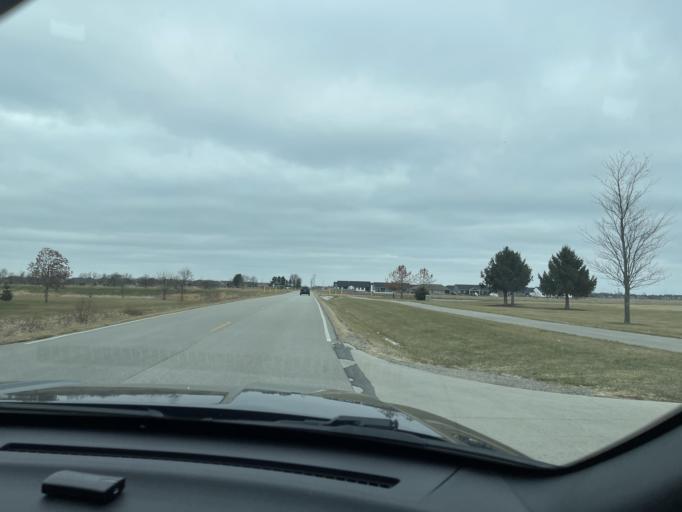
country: US
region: Illinois
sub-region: Sangamon County
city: Jerome
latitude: 39.7587
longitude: -89.7532
